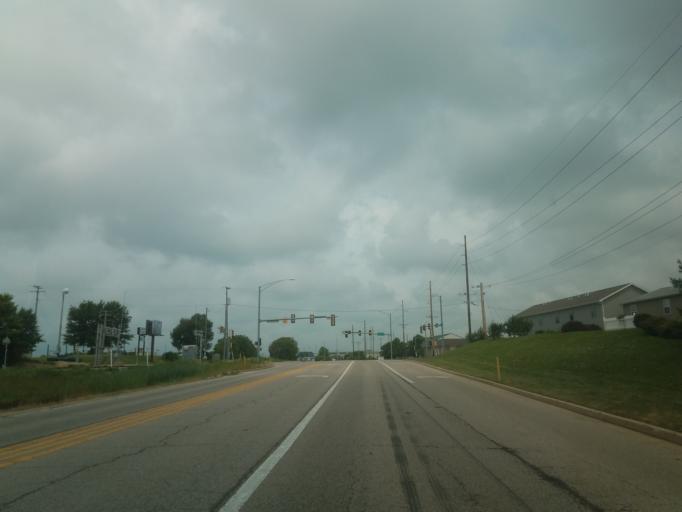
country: US
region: Illinois
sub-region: McLean County
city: Bloomington
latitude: 40.4943
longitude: -89.0197
